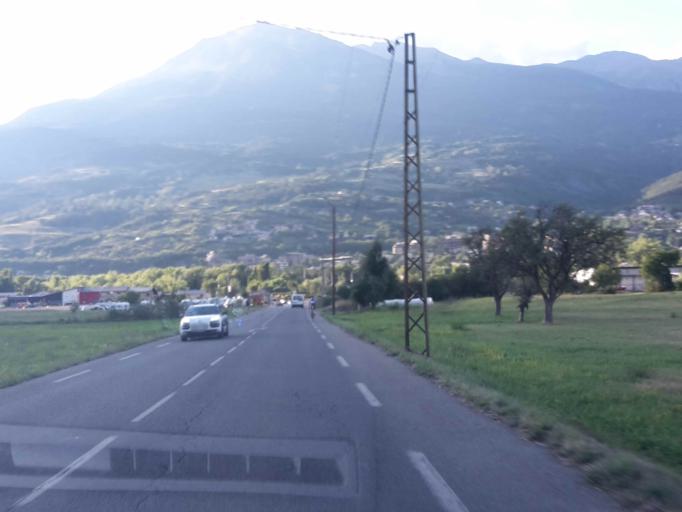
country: FR
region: Provence-Alpes-Cote d'Azur
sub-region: Departement des Hautes-Alpes
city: Embrun
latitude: 44.5459
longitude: 6.4875
